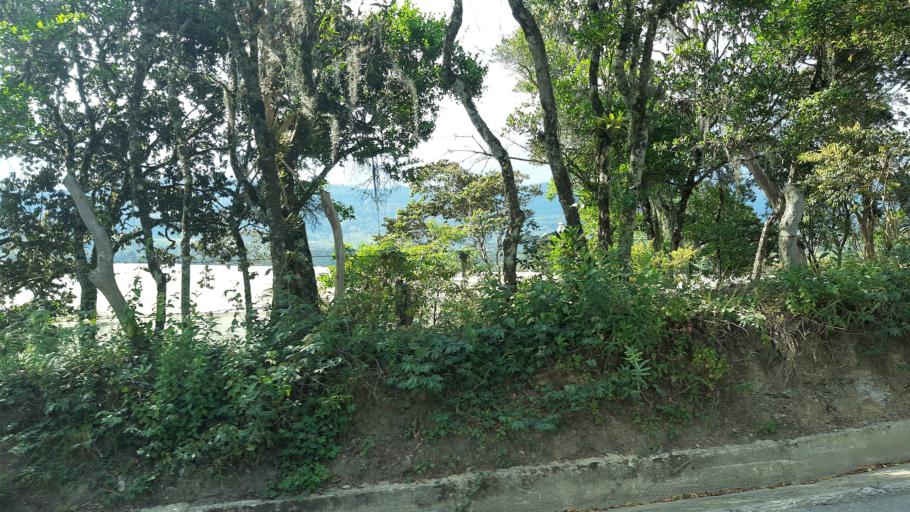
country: CO
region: Boyaca
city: Moniquira
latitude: 5.7986
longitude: -73.6009
